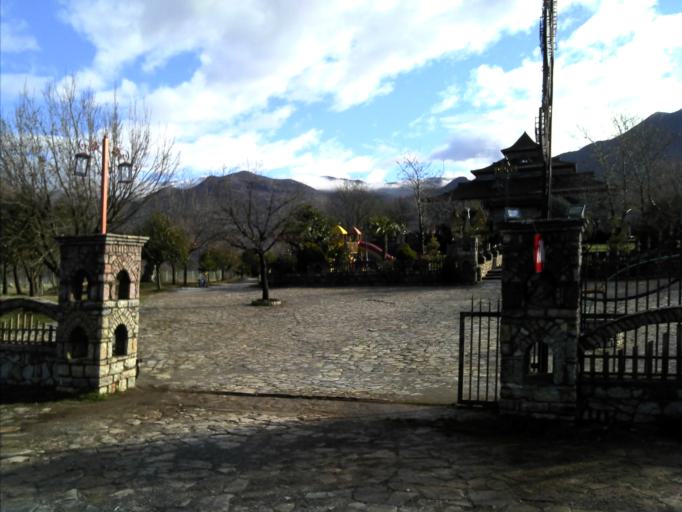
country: AL
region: Shkoder
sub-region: Rrethi i Malesia e Madhe
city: Hot
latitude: 42.2978
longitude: 19.4456
